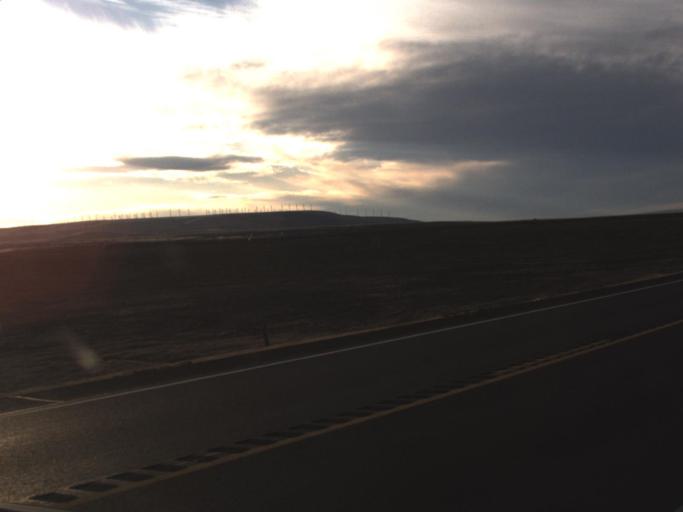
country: US
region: Washington
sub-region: Walla Walla County
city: Burbank
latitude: 46.0611
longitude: -118.7387
